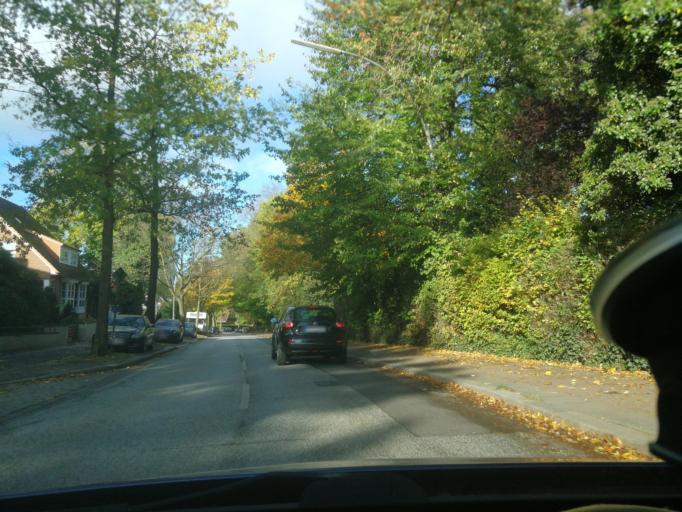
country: DE
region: Hamburg
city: Harburg
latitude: 53.4646
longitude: 9.9556
